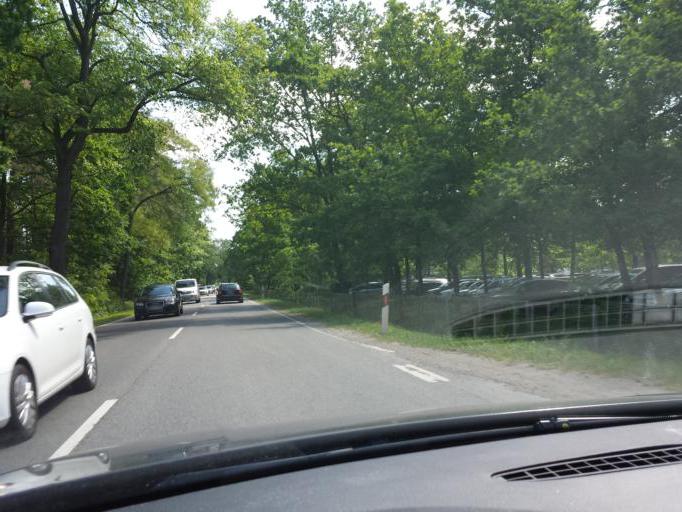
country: DE
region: Brandenburg
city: Leegebruch
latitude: 52.7477
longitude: 13.1547
